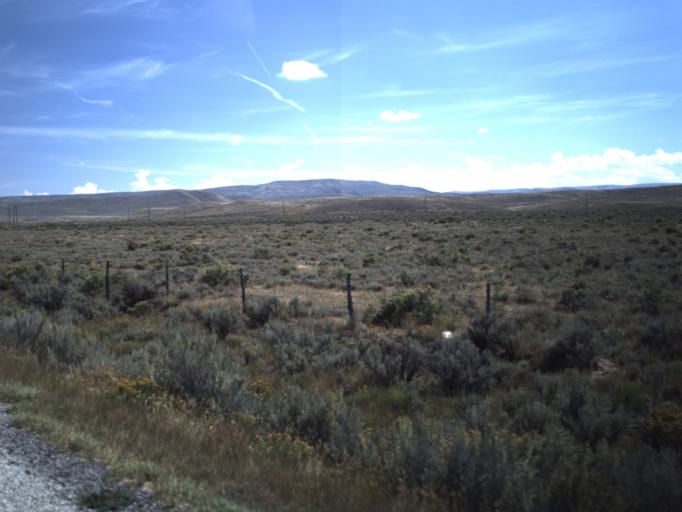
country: US
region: Utah
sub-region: Rich County
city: Randolph
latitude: 41.7790
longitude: -111.0532
